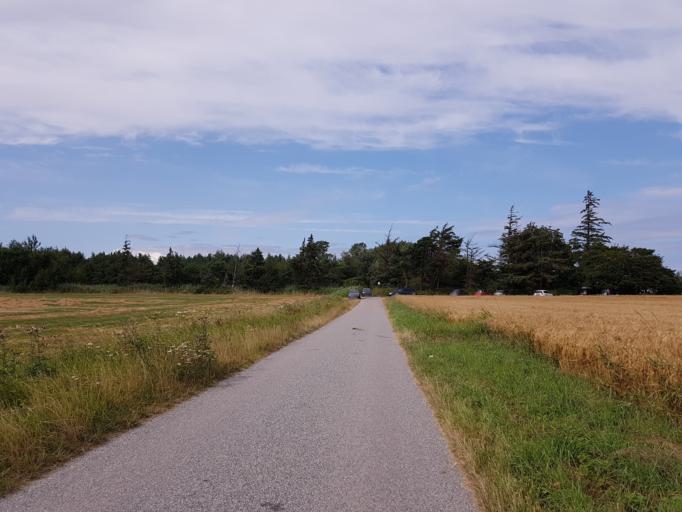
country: DK
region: Zealand
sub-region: Guldborgsund Kommune
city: Nykobing Falster
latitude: 54.5786
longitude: 11.9699
